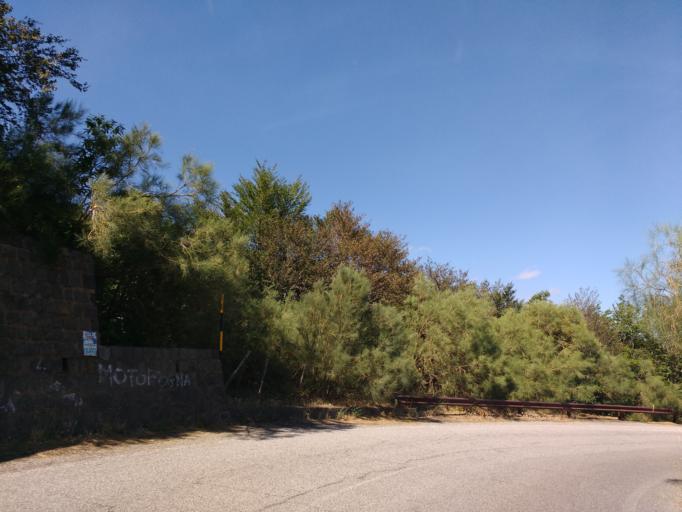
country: IT
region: Sicily
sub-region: Catania
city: Zafferana Etnea
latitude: 37.7009
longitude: 15.0416
